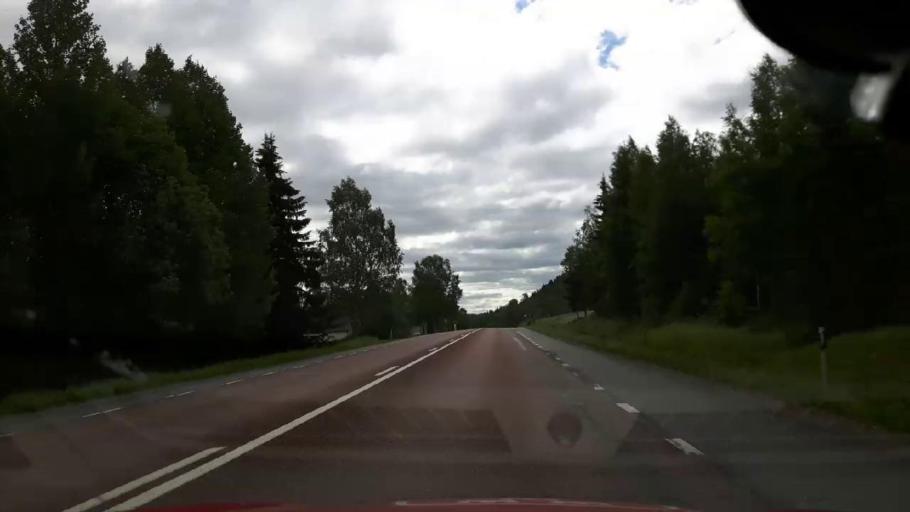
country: SE
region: Jaemtland
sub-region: Braecke Kommun
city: Braecke
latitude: 62.9288
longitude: 15.2225
